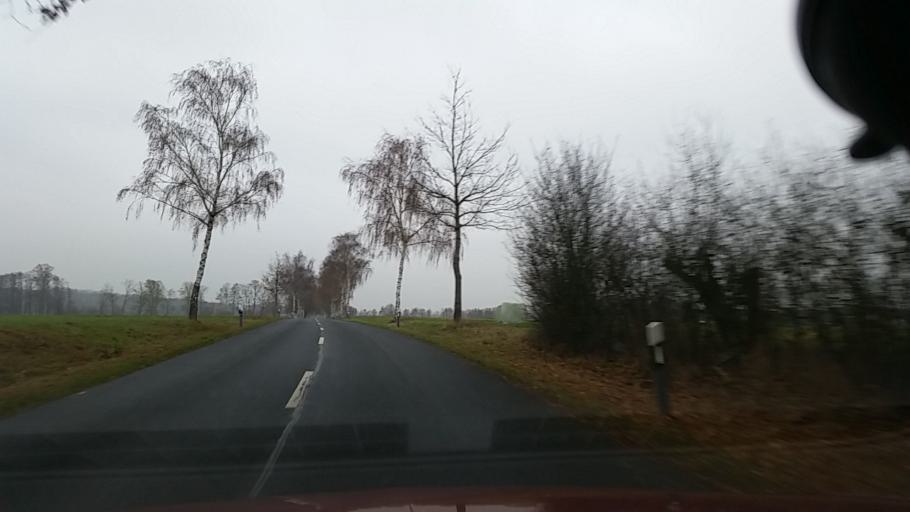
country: DE
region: Lower Saxony
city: Stadensen
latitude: 52.8555
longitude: 10.5702
